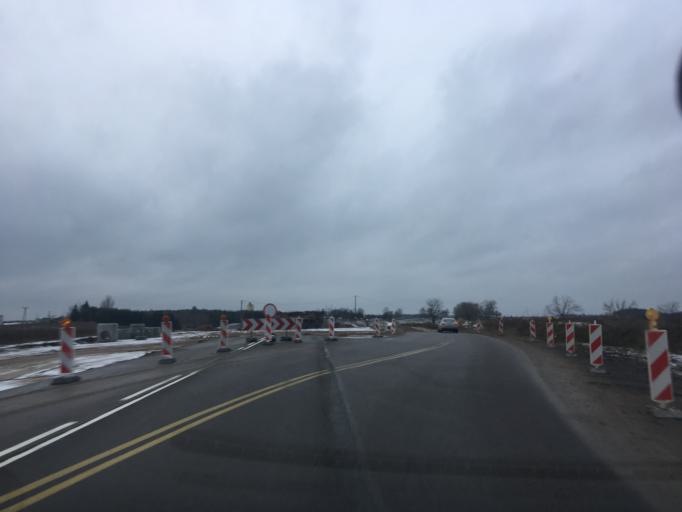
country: PL
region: Podlasie
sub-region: Suwalki
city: Suwalki
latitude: 54.1083
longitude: 22.8783
